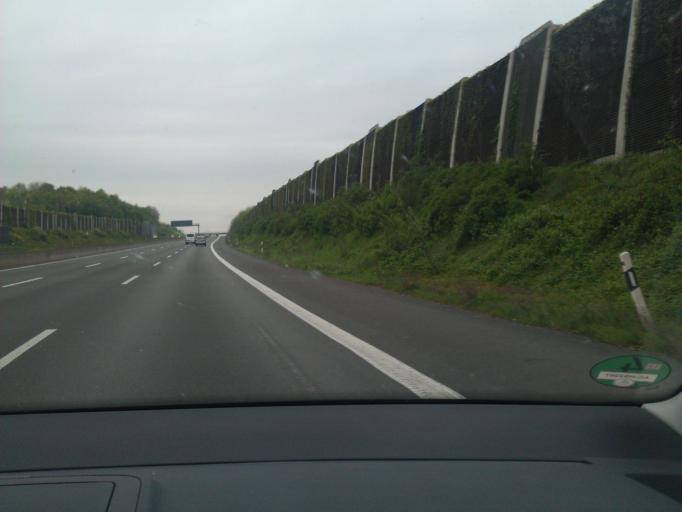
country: DE
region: North Rhine-Westphalia
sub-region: Regierungsbezirk Koln
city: Kerpen
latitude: 50.9032
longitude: 6.7156
